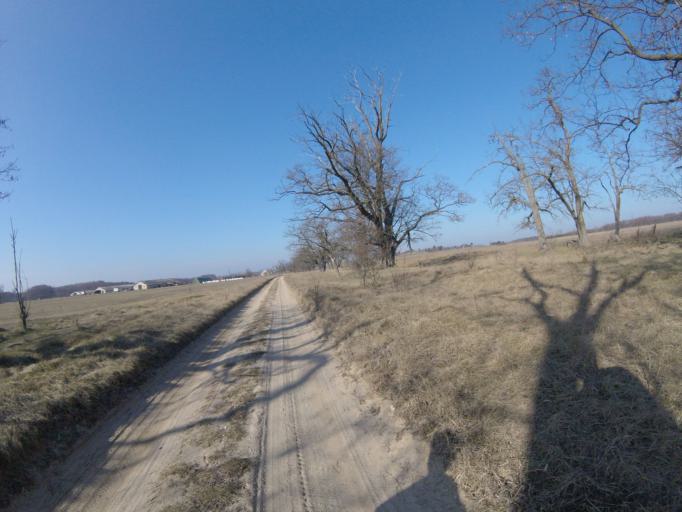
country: HU
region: Komarom-Esztergom
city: Oroszlany
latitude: 47.4683
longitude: 18.3388
